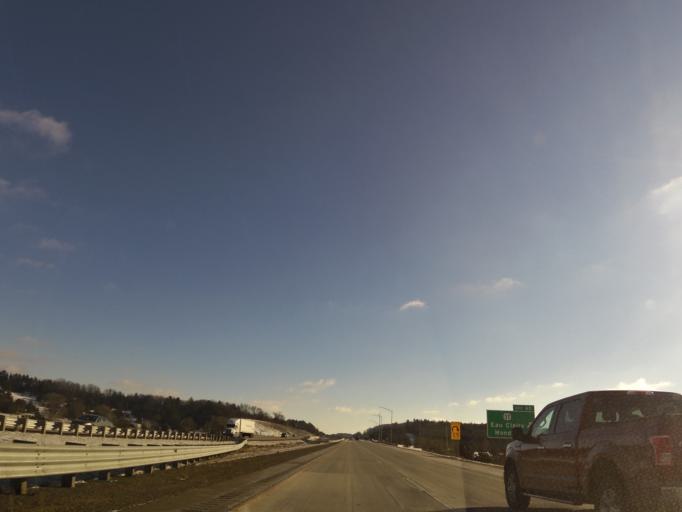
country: US
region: Wisconsin
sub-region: Eau Claire County
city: Eau Claire
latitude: 44.7794
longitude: -91.5358
